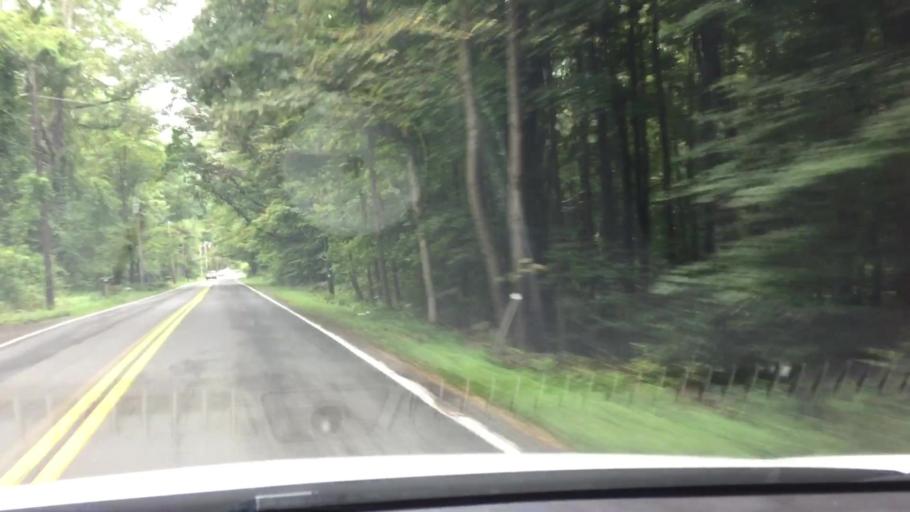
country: US
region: Massachusetts
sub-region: Berkshire County
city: Housatonic
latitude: 42.2362
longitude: -73.3707
